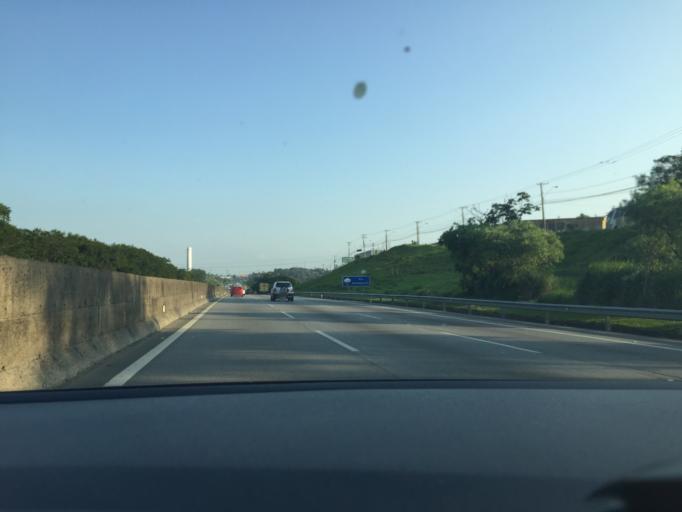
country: BR
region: Sao Paulo
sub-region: Louveira
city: Louveira
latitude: -23.1008
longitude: -46.9660
